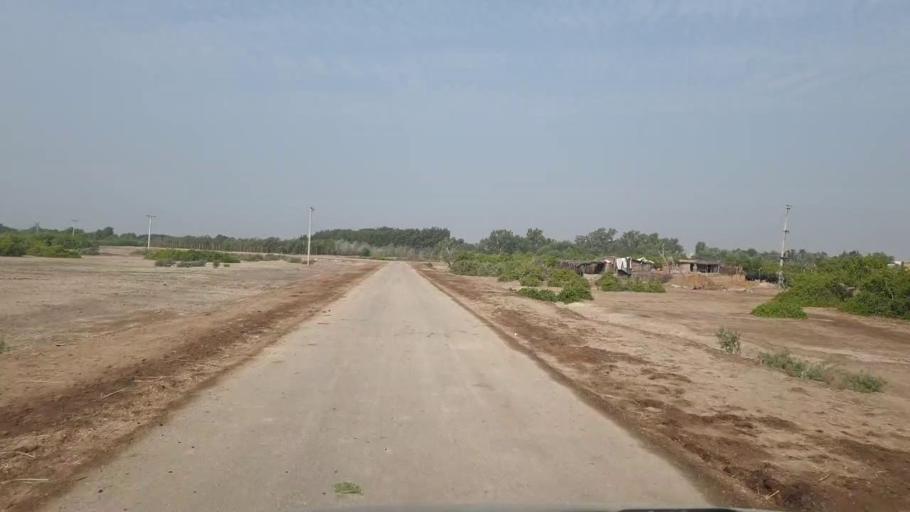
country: PK
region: Sindh
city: Tando Muhammad Khan
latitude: 25.1272
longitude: 68.4564
